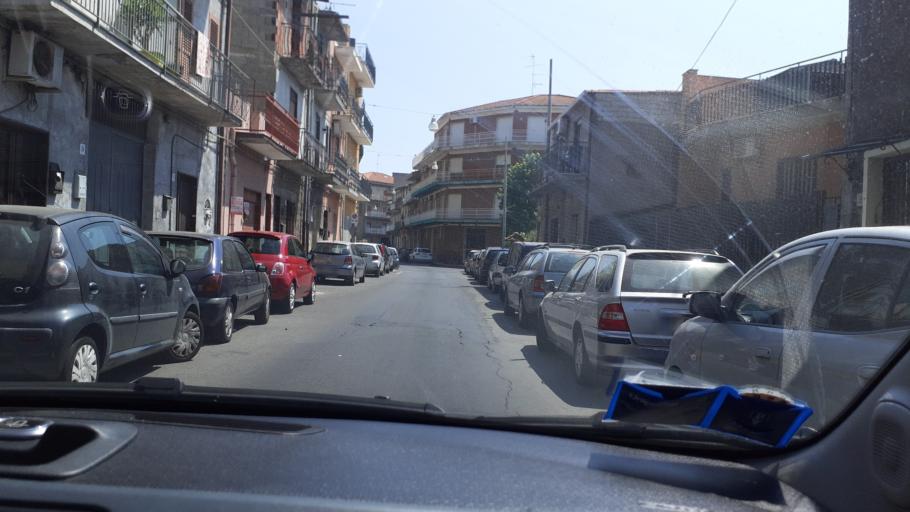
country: IT
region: Sicily
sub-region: Catania
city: Misterbianco
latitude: 37.5173
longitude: 15.0165
